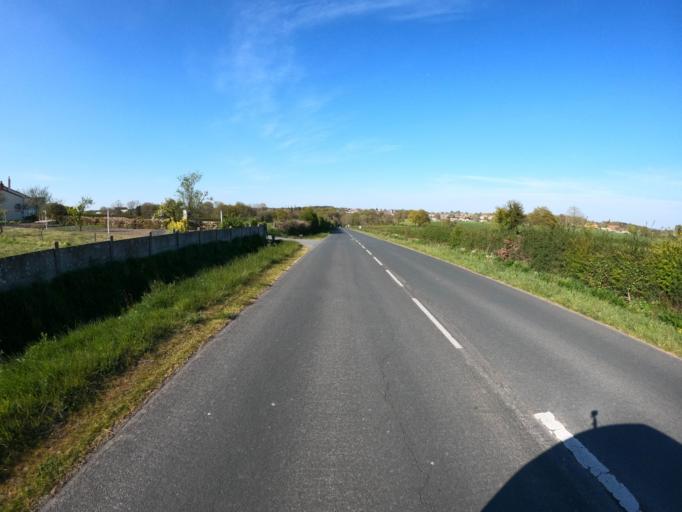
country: FR
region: Pays de la Loire
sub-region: Departement de la Vendee
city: Mortagne-sur-Sevre
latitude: 46.9802
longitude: -0.9644
